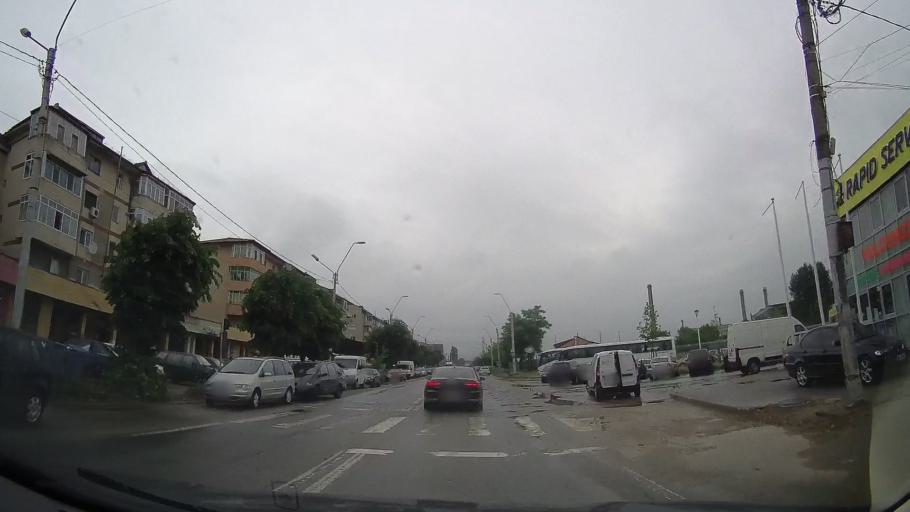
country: RS
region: Central Serbia
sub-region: Borski Okrug
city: Kladovo
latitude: 44.6243
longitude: 22.6159
